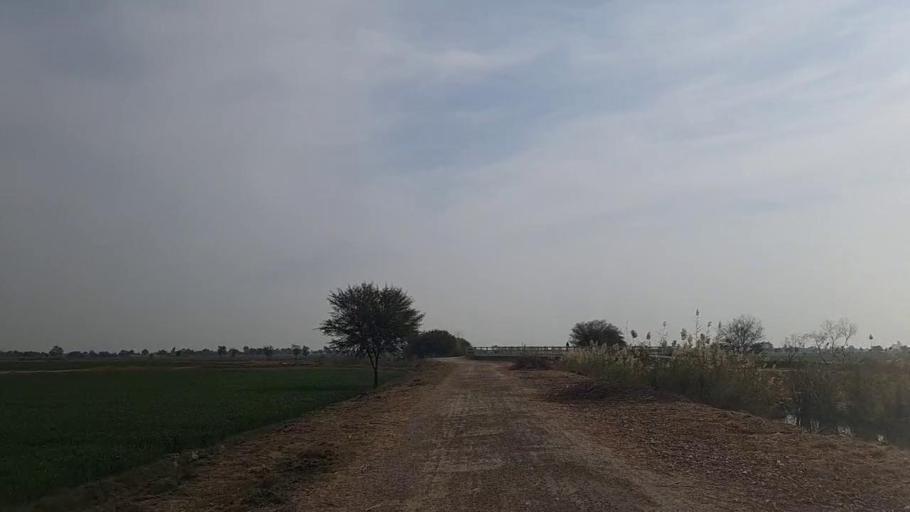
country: PK
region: Sindh
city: Daur
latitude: 26.4443
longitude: 68.4209
